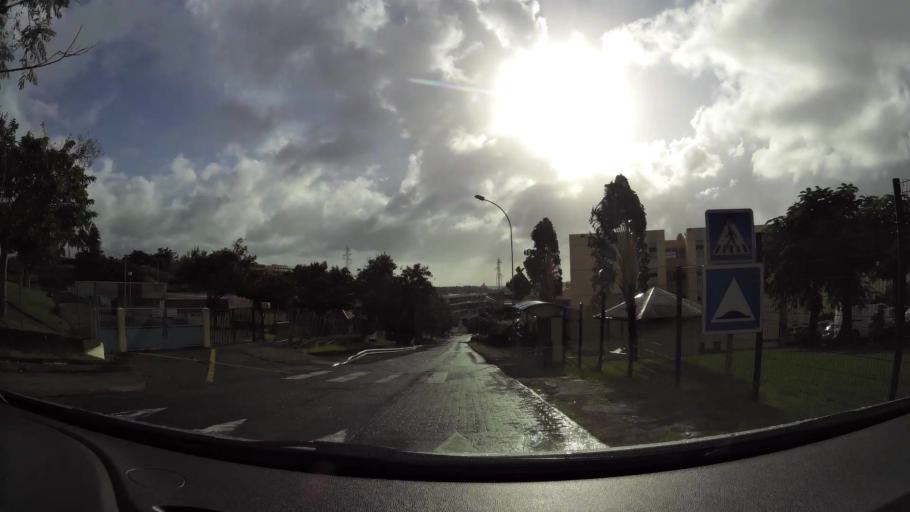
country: MQ
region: Martinique
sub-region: Martinique
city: Fort-de-France
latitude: 14.6183
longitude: -61.0419
